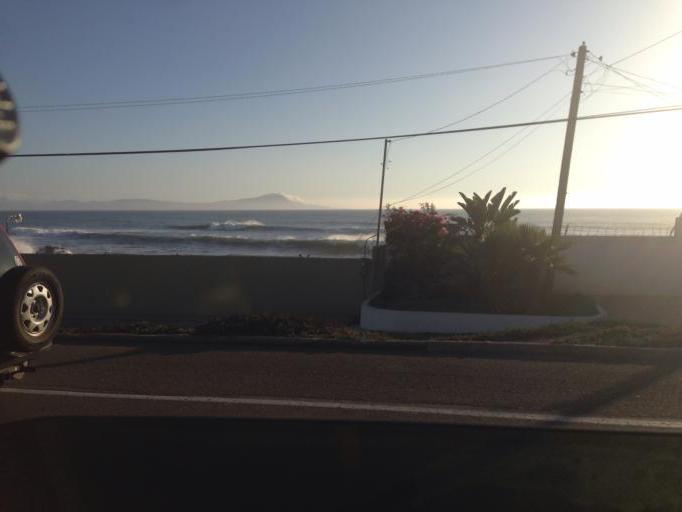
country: MX
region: Baja California
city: El Sauzal
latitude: 31.8692
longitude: -116.6750
